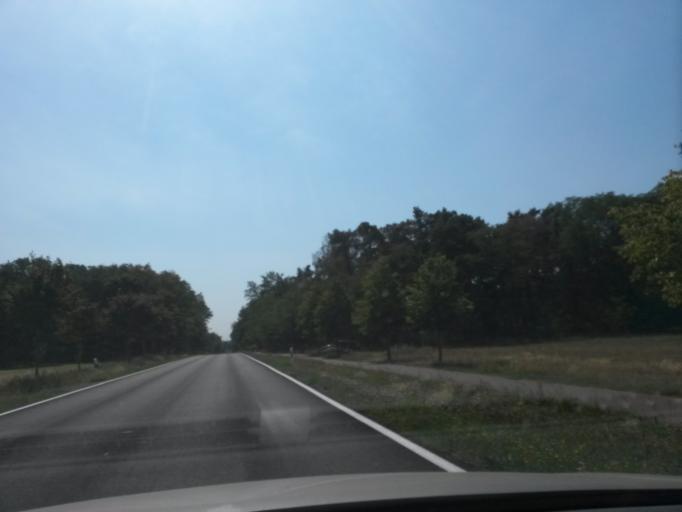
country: DE
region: Saxony-Anhalt
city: Jerichow
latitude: 52.3997
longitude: 11.9958
